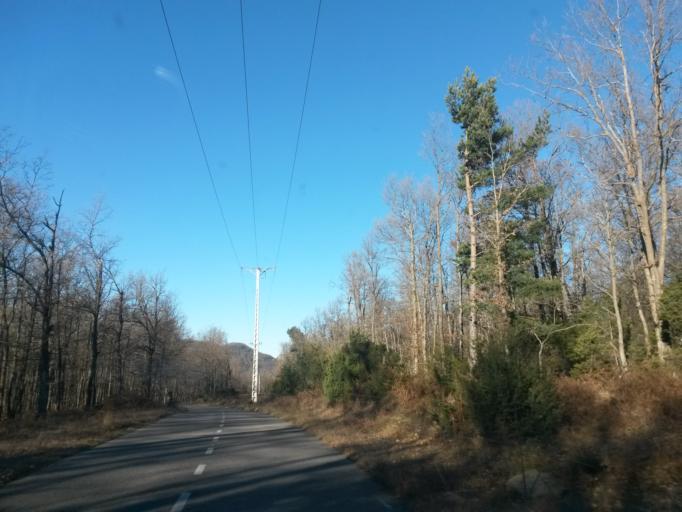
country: ES
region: Catalonia
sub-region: Provincia de Girona
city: les Planes d'Hostoles
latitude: 42.0297
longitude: 2.5253
